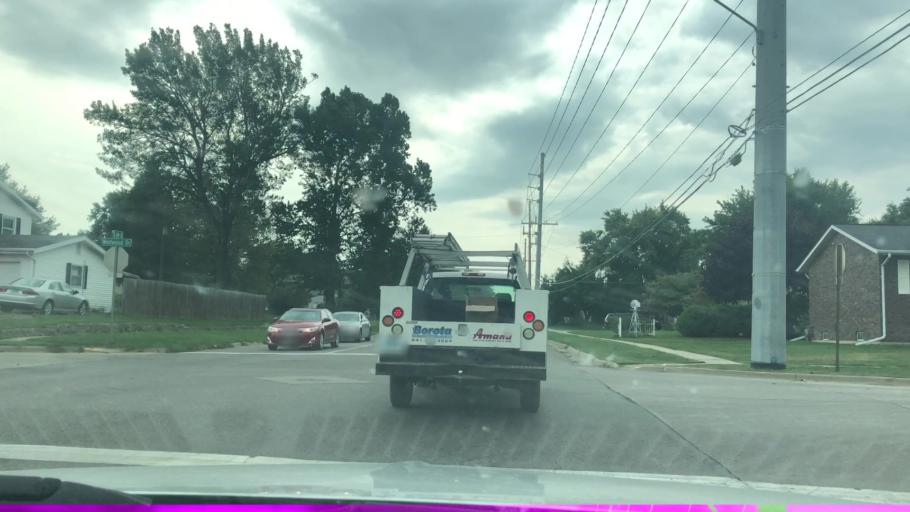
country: US
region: Iowa
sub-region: Marshall County
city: Marshalltown
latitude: 42.0212
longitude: -92.9221
